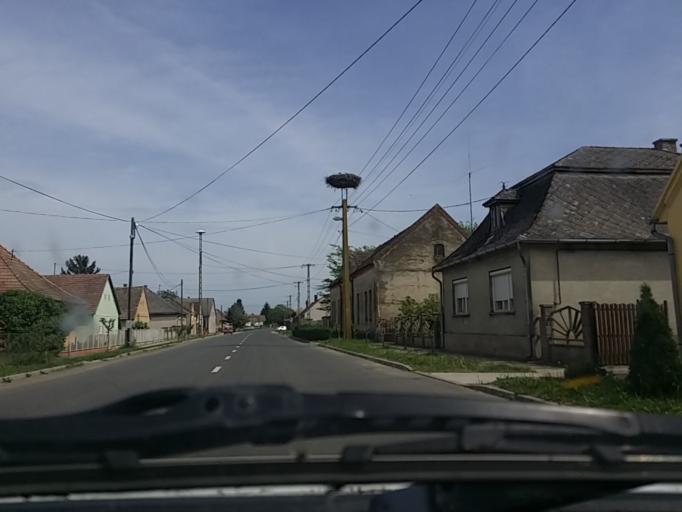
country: HU
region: Baranya
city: Vajszlo
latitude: 45.8561
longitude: 17.9929
